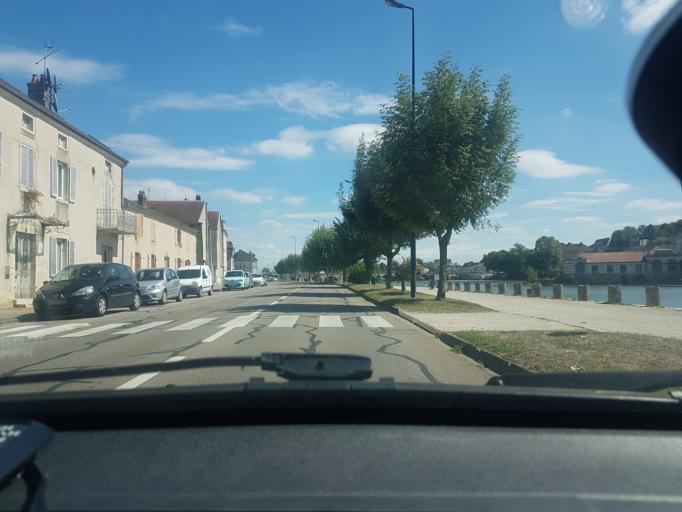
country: FR
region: Franche-Comte
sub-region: Departement de la Haute-Saone
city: Arc-les-Gray
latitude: 47.4506
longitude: 5.5866
